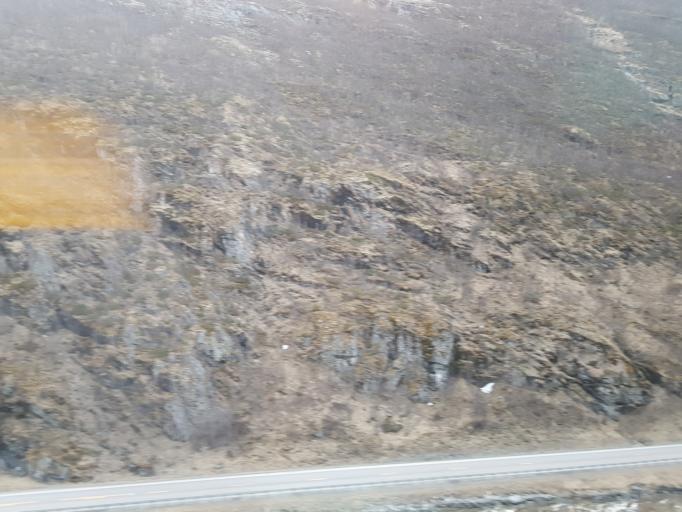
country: NO
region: Sor-Trondelag
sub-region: Oppdal
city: Oppdal
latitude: 62.3394
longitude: 9.6188
